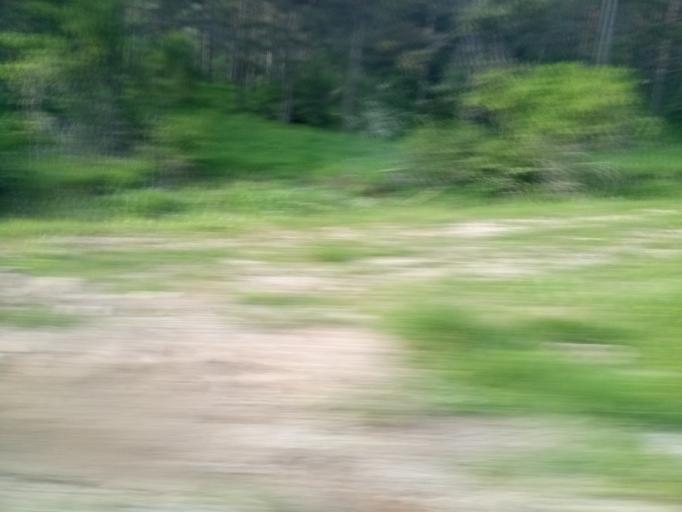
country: TR
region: Karabuk
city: Eskipazar
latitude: 41.0457
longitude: 32.5490
